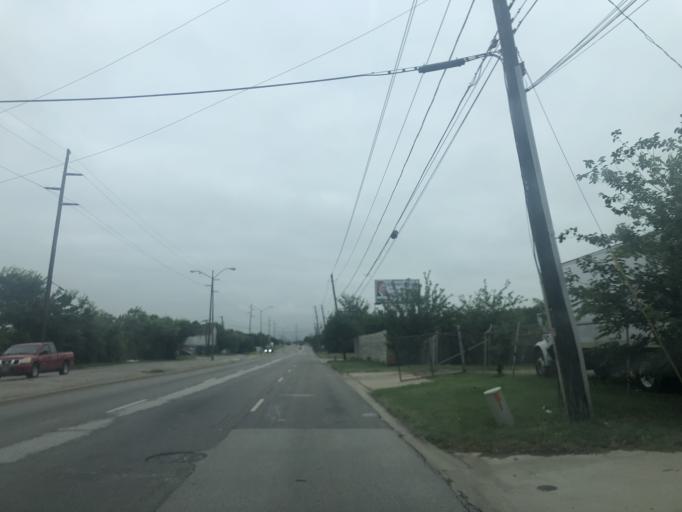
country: US
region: Texas
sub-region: Dallas County
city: Cockrell Hill
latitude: 32.7789
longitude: -96.8760
